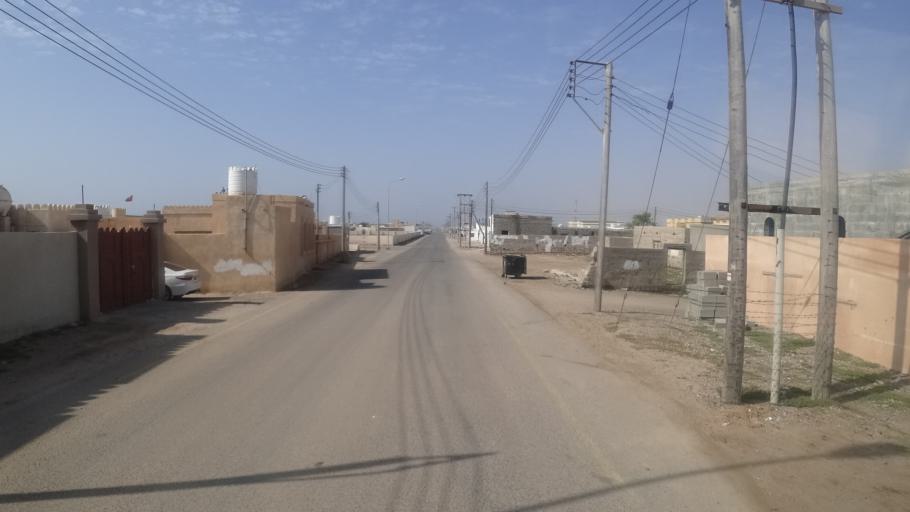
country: OM
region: Ash Sharqiyah
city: Sur
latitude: 22.1826
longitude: 59.7634
